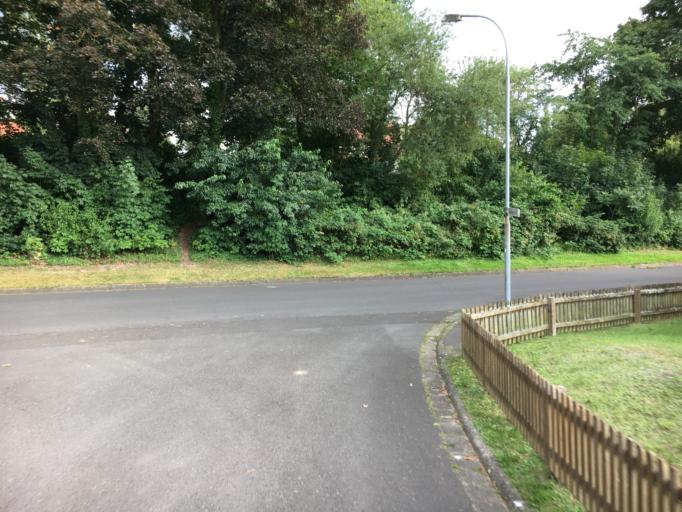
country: DE
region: Hesse
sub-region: Regierungsbezirk Kassel
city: Schrecksbach
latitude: 50.8561
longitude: 9.2928
